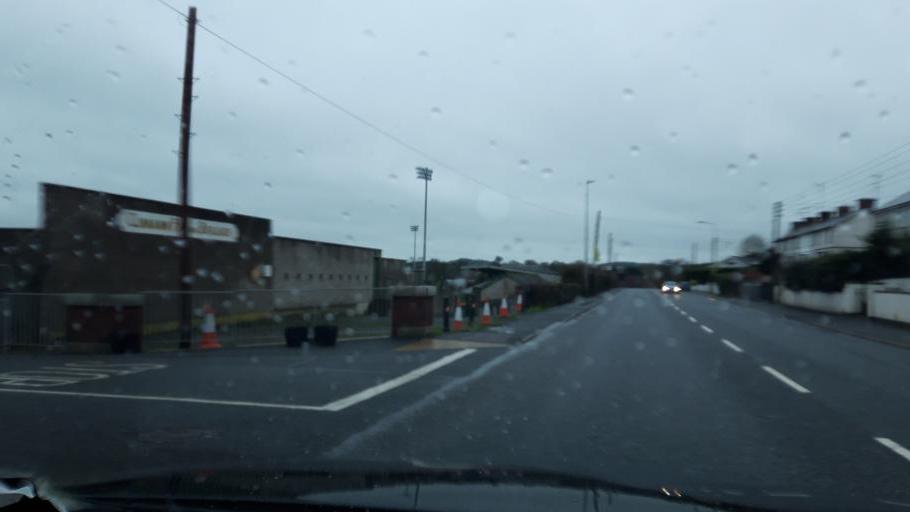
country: IE
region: Ulster
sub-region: County Monaghan
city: Castleblayney
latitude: 54.1143
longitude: -6.7329
